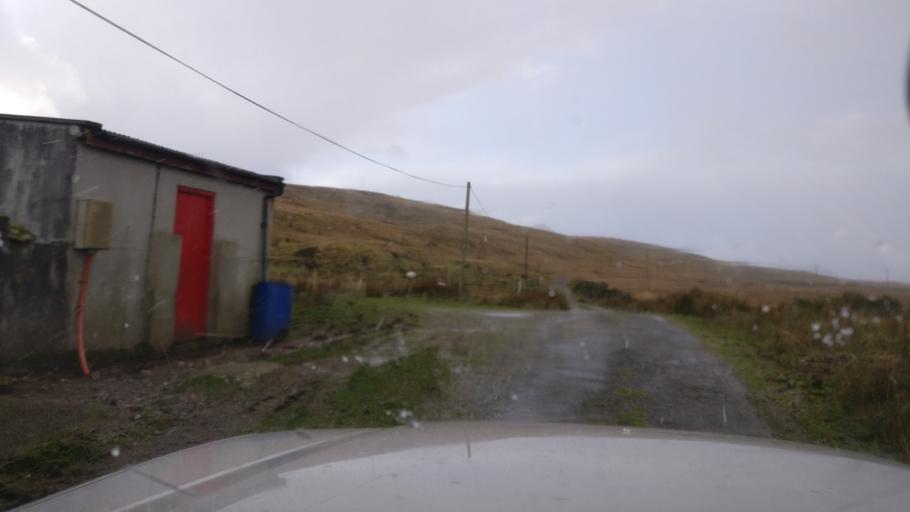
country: IE
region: Connaught
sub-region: County Galway
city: Clifden
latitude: 53.4915
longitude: -9.7001
